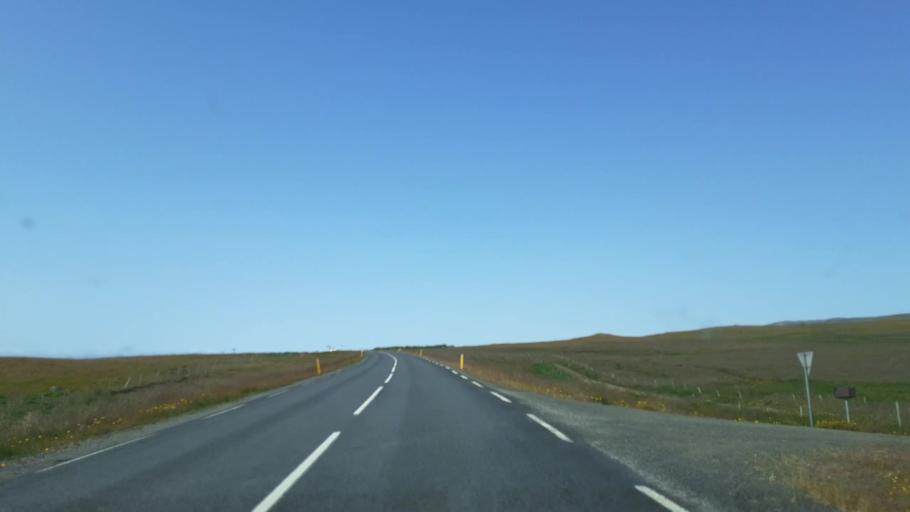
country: IS
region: Northwest
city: Saudarkrokur
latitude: 65.3599
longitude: -20.8908
